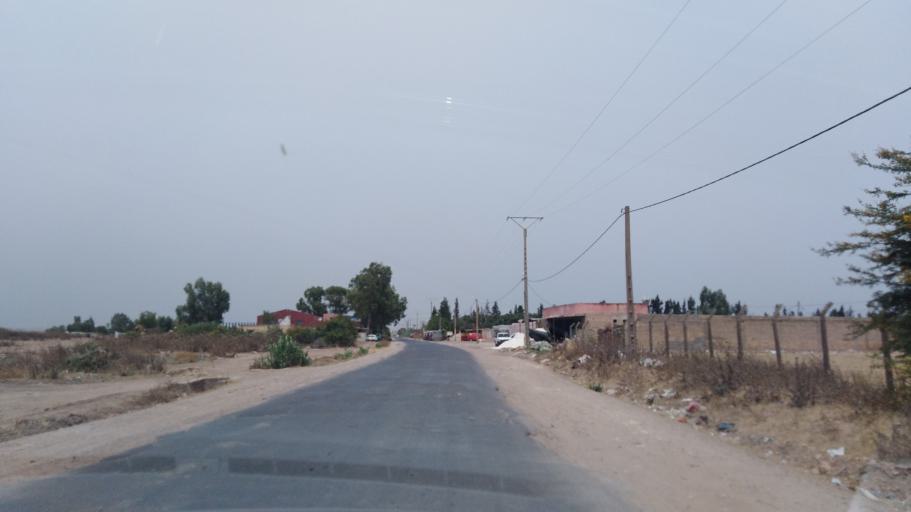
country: MA
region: Grand Casablanca
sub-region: Mediouna
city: Mediouna
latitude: 33.4060
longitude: -7.5135
